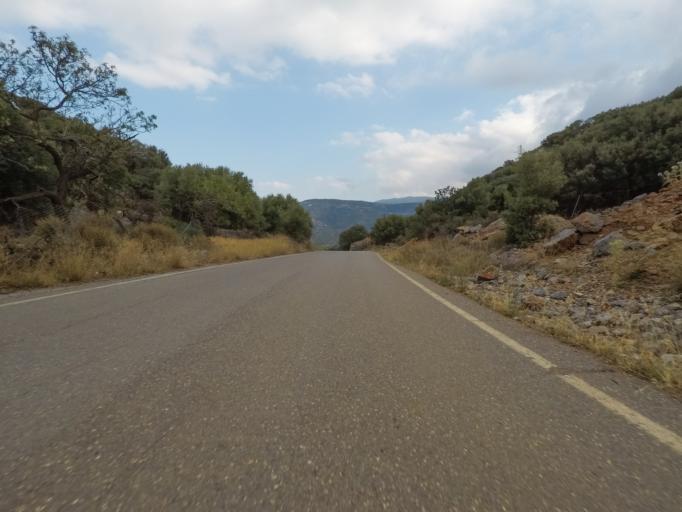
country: GR
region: Crete
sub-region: Nomos Lasithiou
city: Kritsa
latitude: 35.1689
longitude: 25.6546
